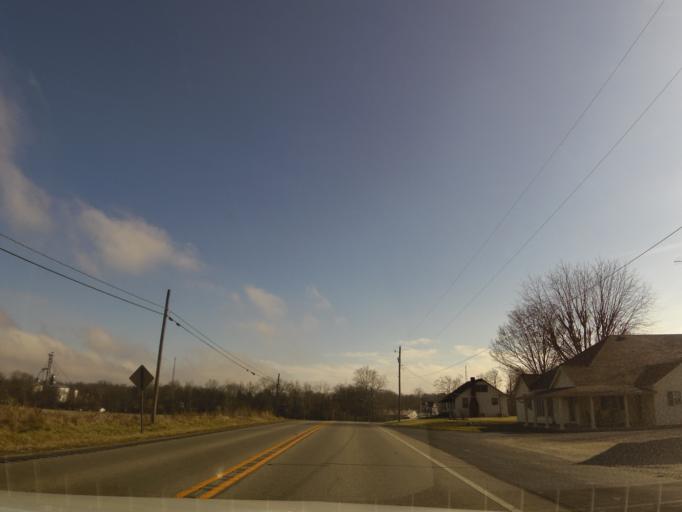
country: US
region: Indiana
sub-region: Jennings County
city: North Vernon
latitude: 38.8908
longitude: -85.5232
